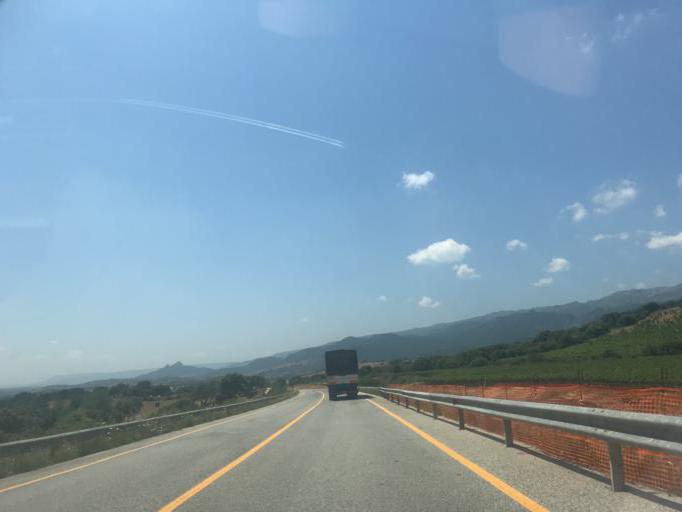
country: IT
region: Sardinia
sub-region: Provincia di Olbia-Tempio
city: Berchidda
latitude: 40.7810
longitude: 9.2224
